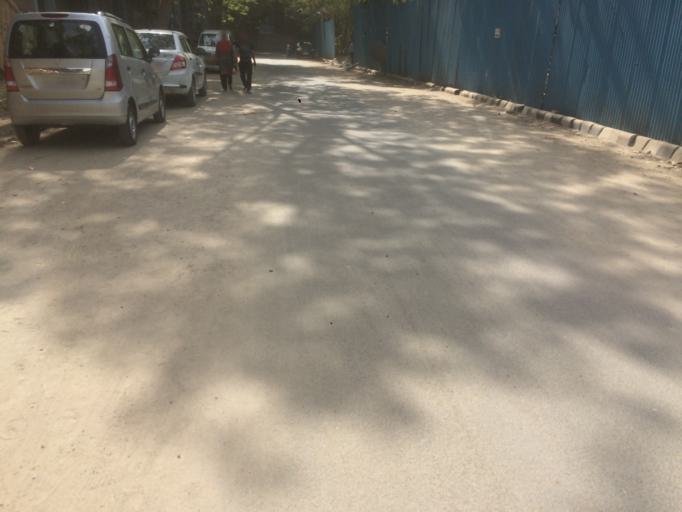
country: IN
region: NCT
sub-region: New Delhi
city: New Delhi
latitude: 28.6350
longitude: 77.2110
